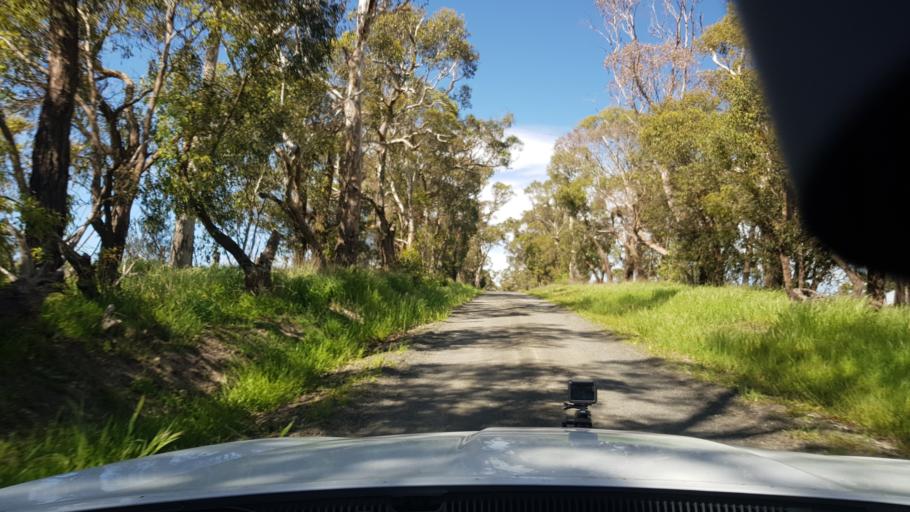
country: AU
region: Victoria
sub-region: Latrobe
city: Moe
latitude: -38.1523
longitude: 146.1369
